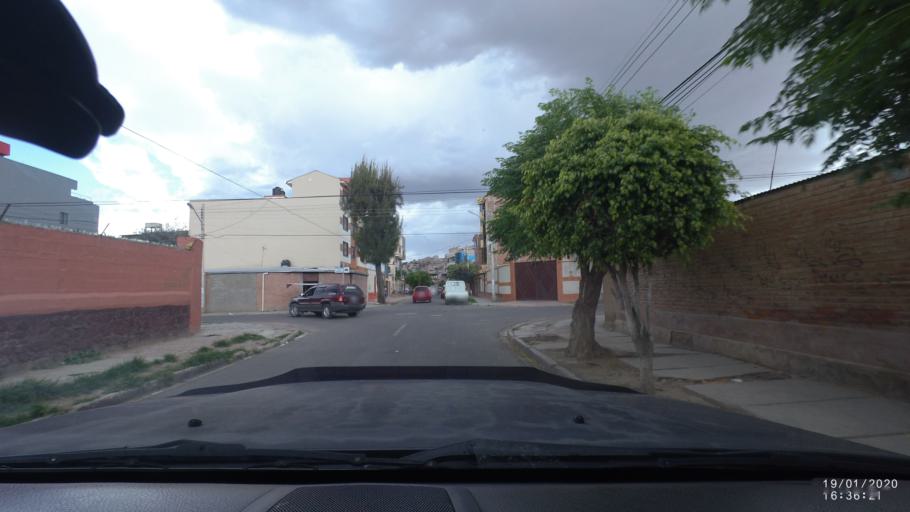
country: BO
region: Cochabamba
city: Cochabamba
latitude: -17.4144
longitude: -66.1579
